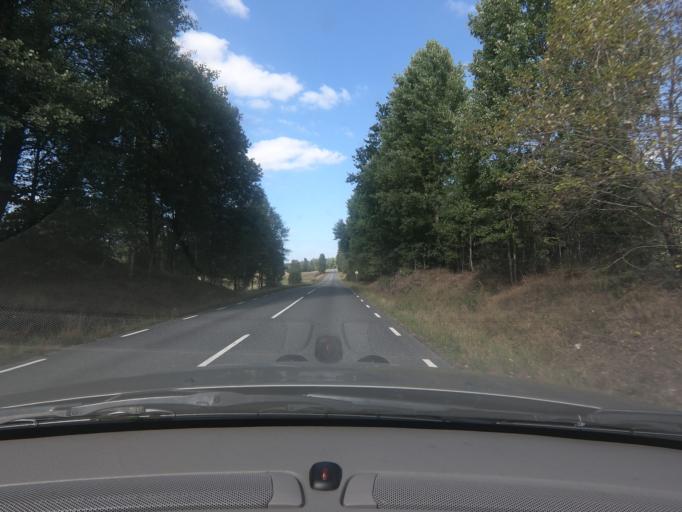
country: SE
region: Joenkoeping
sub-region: Vetlanda Kommun
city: Landsbro
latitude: 57.3362
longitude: 14.8702
